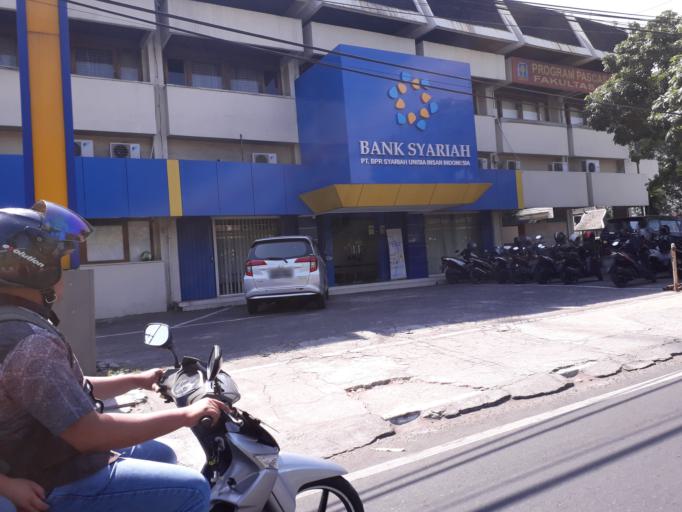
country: ID
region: Daerah Istimewa Yogyakarta
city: Yogyakarta
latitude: -7.7824
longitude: 110.3751
